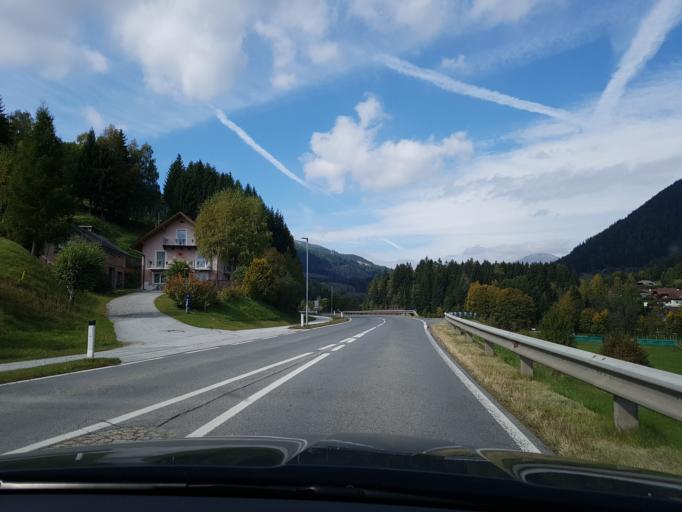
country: AT
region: Carinthia
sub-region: Politischer Bezirk Feldkirchen
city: Gnesau
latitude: 46.7776
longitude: 13.9536
